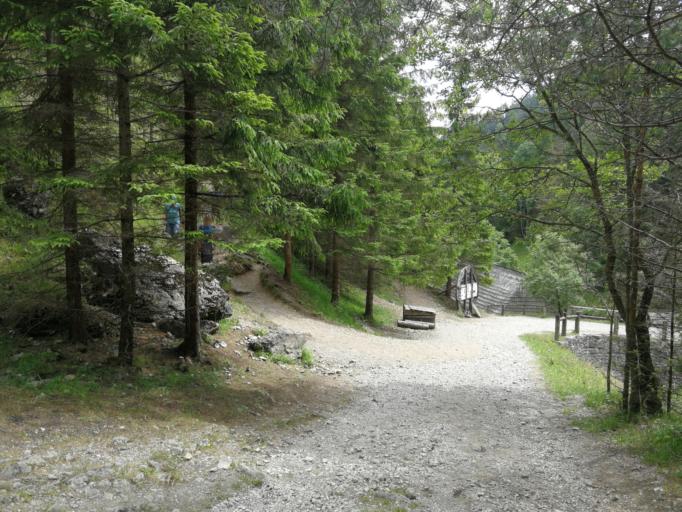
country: SK
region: Zilinsky
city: Tvrdosin
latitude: 49.1967
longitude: 19.5411
